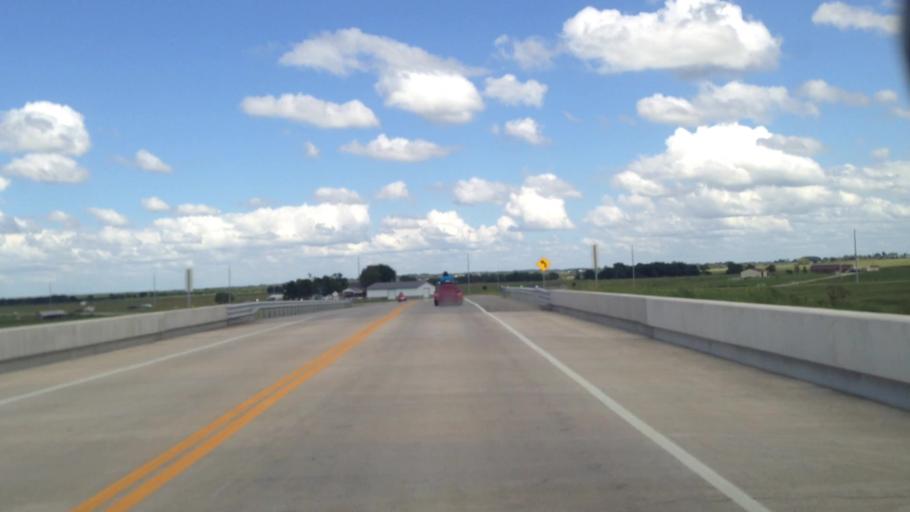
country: US
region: Kansas
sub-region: Labette County
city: Chetopa
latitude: 36.8910
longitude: -95.0942
